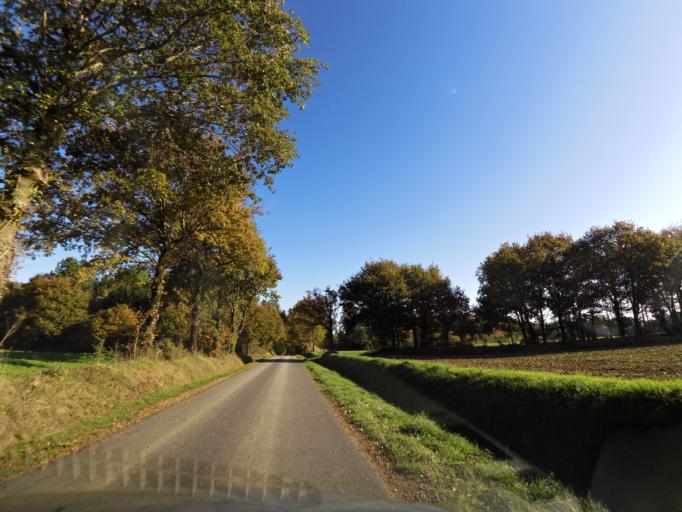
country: FR
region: Brittany
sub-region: Departement d'Ille-et-Vilaine
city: Bain-de-Bretagne
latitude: 47.8715
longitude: -1.7041
